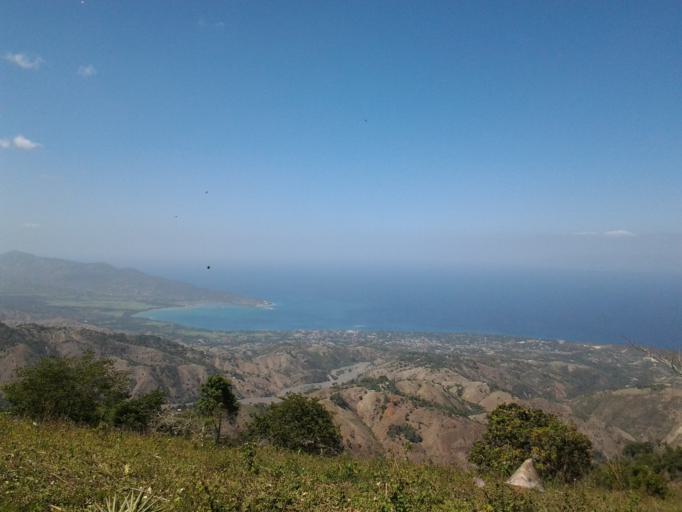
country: HT
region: Ouest
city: Tigwav
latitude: 18.3881
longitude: -72.8212
